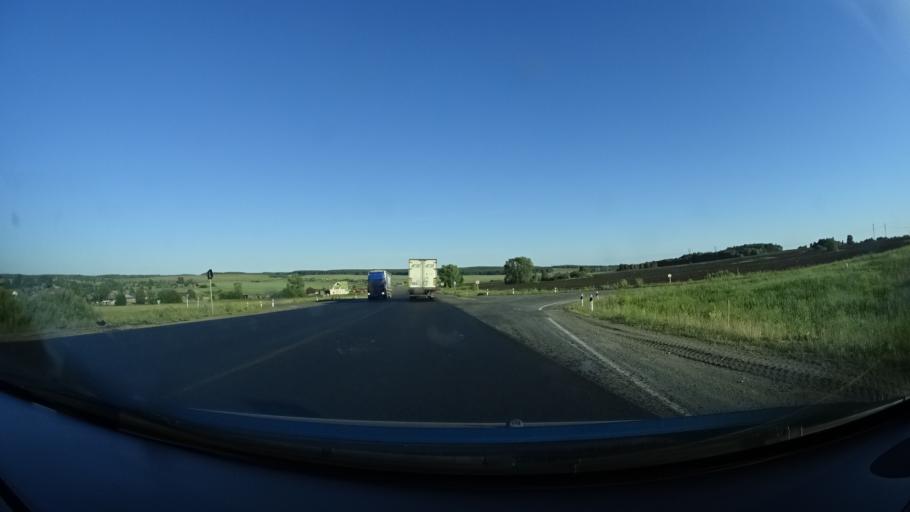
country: RU
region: Sverdlovsk
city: Achit
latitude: 56.8955
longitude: 57.6039
